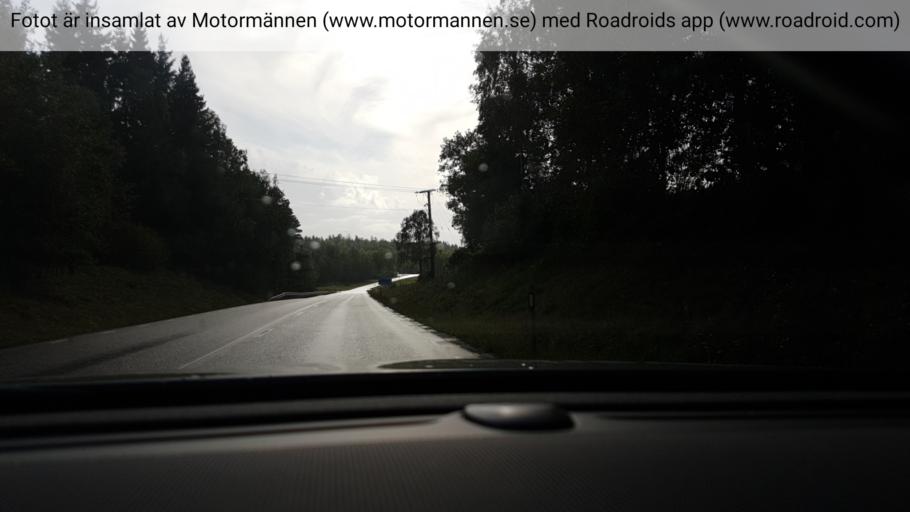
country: SE
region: Vaestra Goetaland
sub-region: Vargarda Kommun
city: Jonstorp
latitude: 58.0698
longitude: 12.6853
